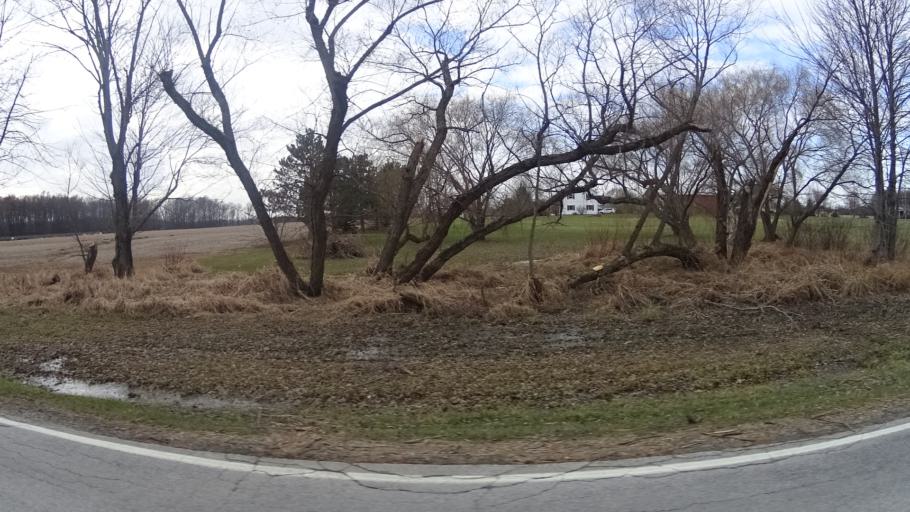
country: US
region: Ohio
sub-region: Lorain County
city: Camden
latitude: 41.2577
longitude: -82.3312
